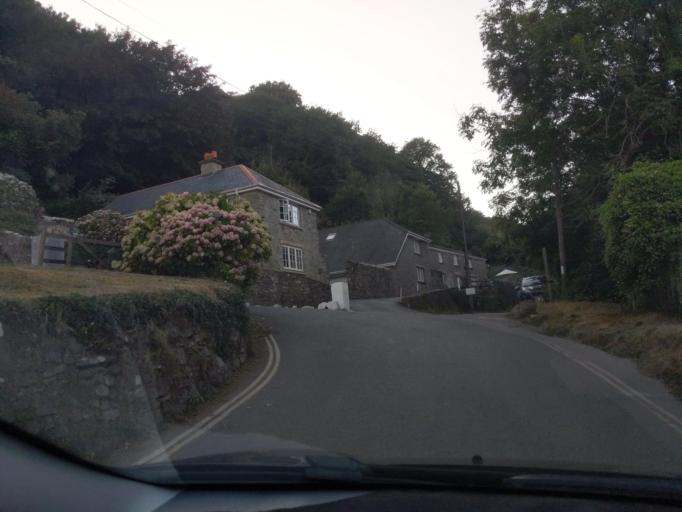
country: GB
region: England
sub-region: Devon
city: Salcombe
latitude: 50.2297
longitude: -3.7824
